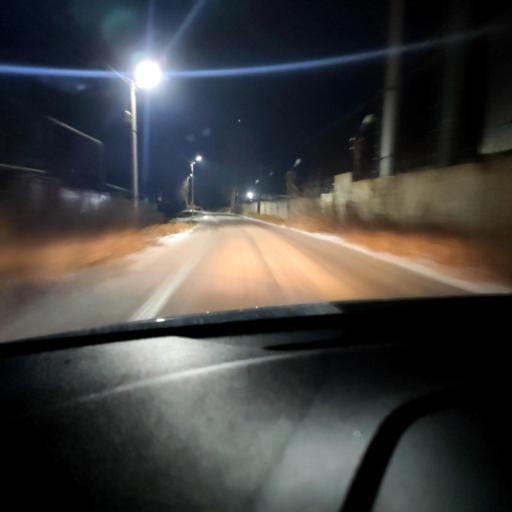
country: RU
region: Tatarstan
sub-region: Gorod Kazan'
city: Kazan
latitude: 55.7229
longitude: 49.0988
